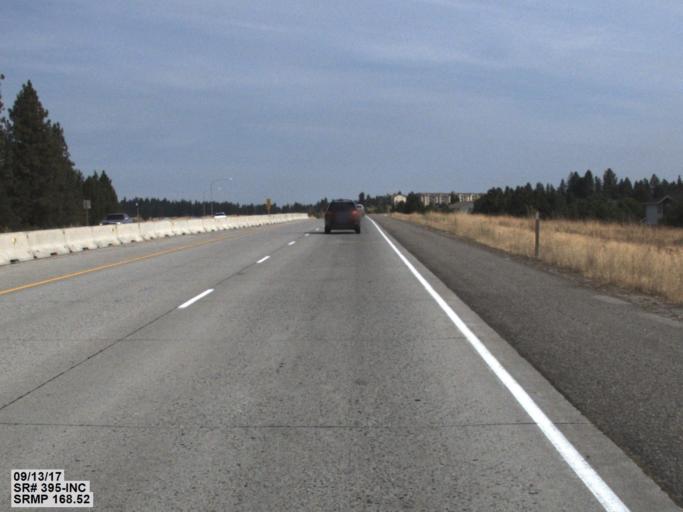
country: US
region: Washington
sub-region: Spokane County
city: Fairwood
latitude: 47.7959
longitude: -117.4070
